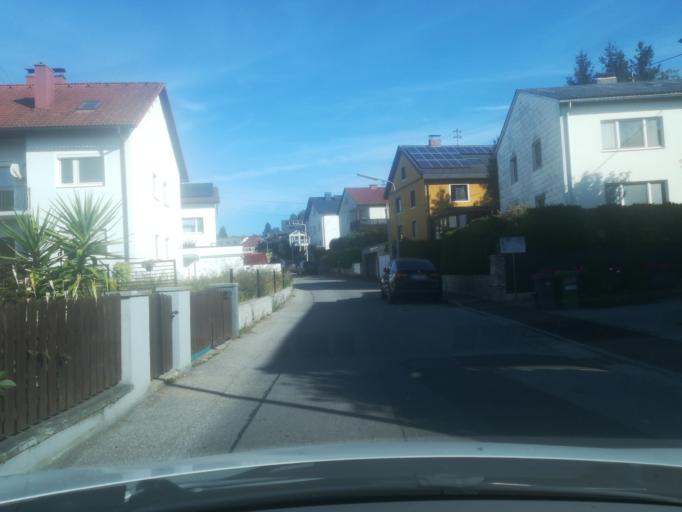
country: AT
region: Upper Austria
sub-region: Politischer Bezirk Linz-Land
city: Leonding
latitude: 48.2761
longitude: 14.2590
